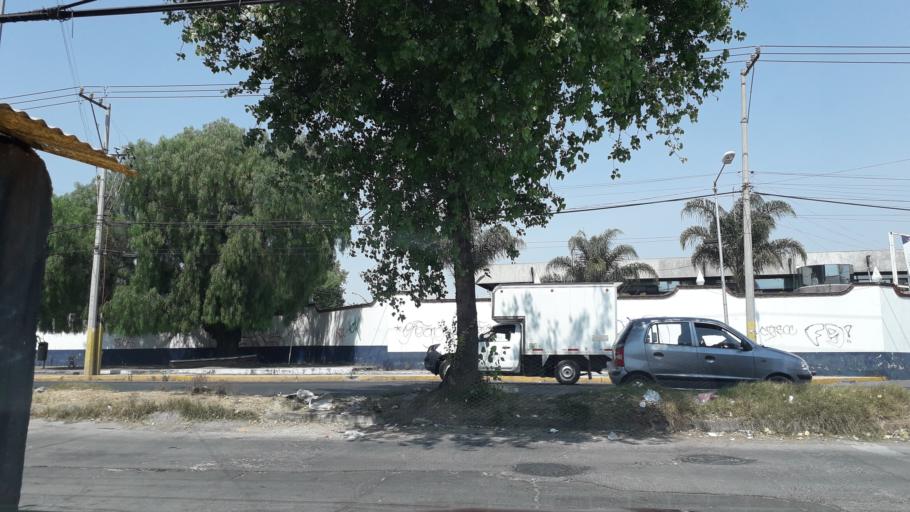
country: MX
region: Puebla
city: Puebla
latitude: 19.0778
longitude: -98.2170
